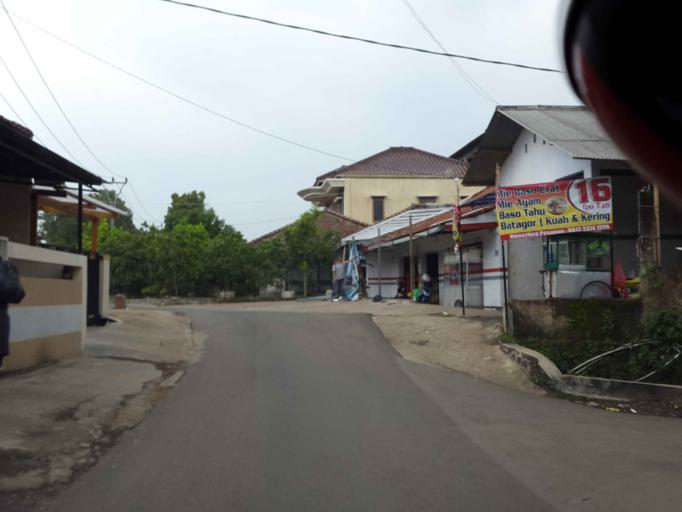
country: ID
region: West Java
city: Lembang
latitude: -6.8293
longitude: 107.5842
